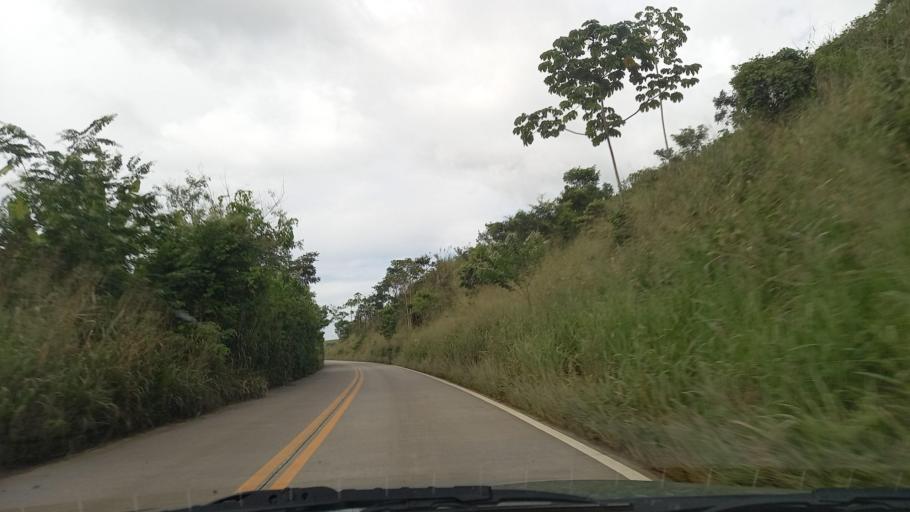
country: BR
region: Pernambuco
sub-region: Maraial
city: Maraial
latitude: -8.7617
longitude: -35.8573
